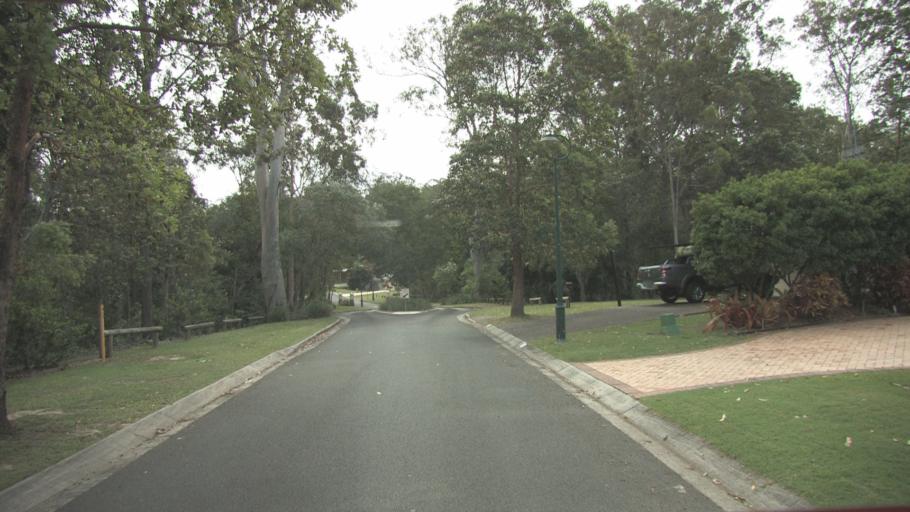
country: AU
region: Queensland
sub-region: Logan
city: Slacks Creek
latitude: -27.6551
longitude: 153.2002
